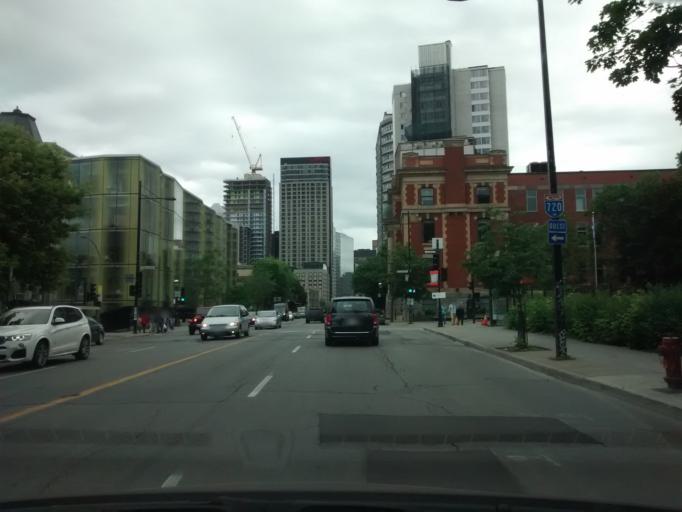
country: CA
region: Quebec
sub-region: Montreal
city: Montreal
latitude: 45.5116
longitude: -73.5699
